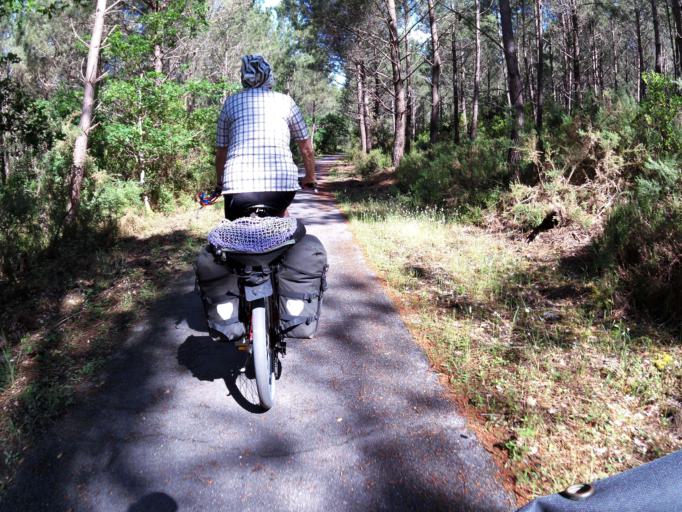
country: FR
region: Aquitaine
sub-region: Departement de la Gironde
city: Lacanau
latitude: 45.0303
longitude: -1.1548
